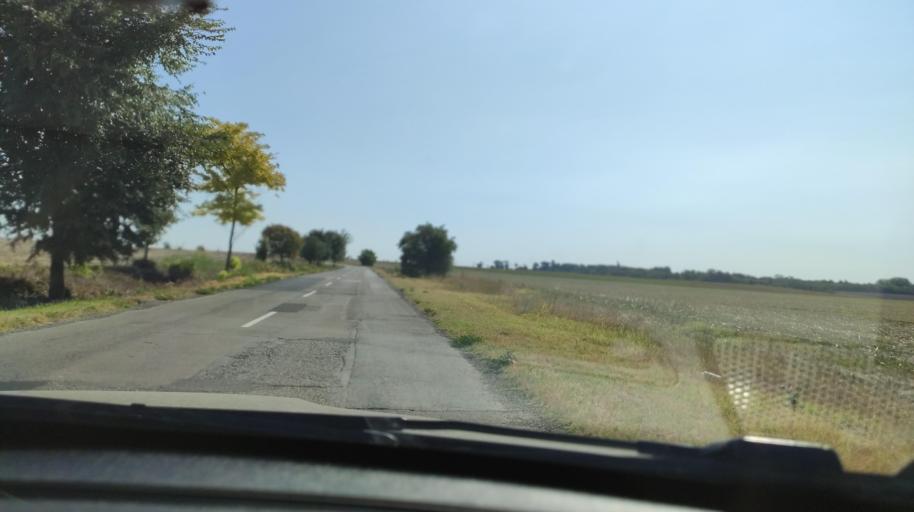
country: RS
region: Autonomna Pokrajina Vojvodina
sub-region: Severnobacki Okrug
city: Backa Topola
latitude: 45.8671
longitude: 19.6190
